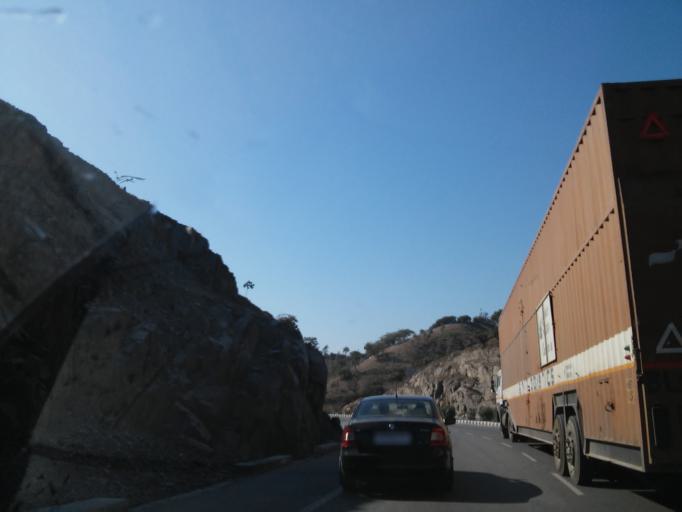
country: IN
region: Rajasthan
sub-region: Udaipur
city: Udaipur
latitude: 24.4392
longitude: 73.6466
